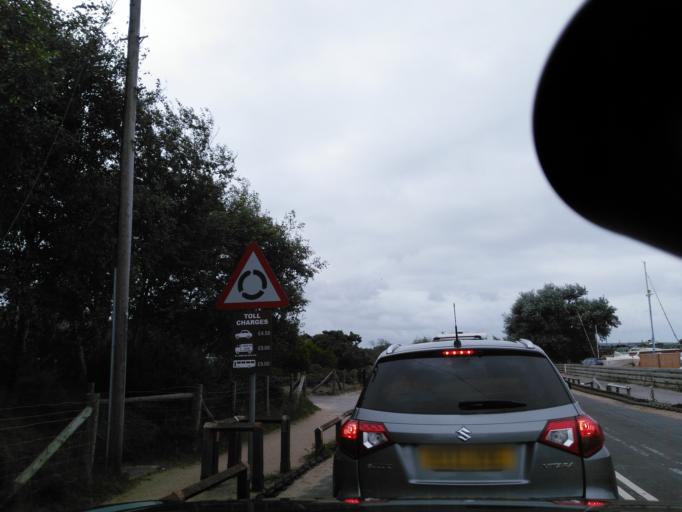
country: GB
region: England
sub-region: Dorset
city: Parkstone
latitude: 50.6780
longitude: -1.9511
